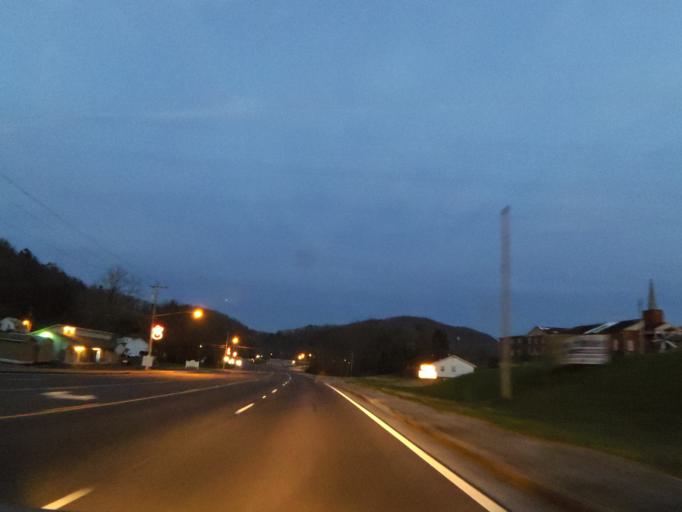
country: US
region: Tennessee
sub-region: Roane County
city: Oliver Springs
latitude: 36.0430
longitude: -84.3528
